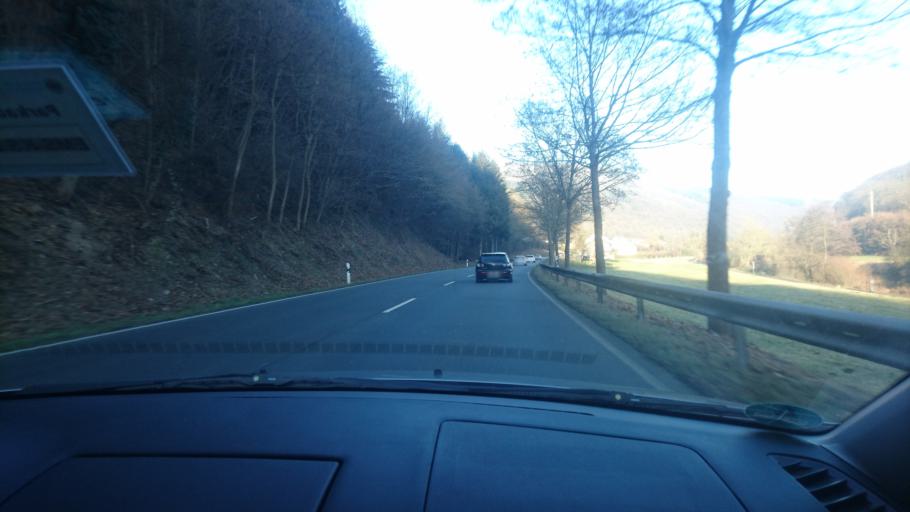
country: DE
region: Rheinland-Pfalz
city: Miellen
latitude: 50.3271
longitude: 7.6647
